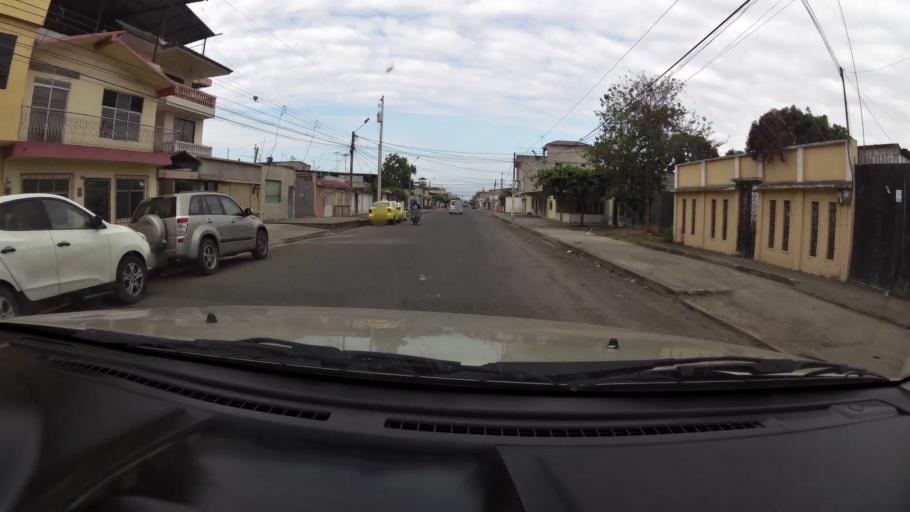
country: EC
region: El Oro
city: Machala
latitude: -3.2519
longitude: -79.9523
